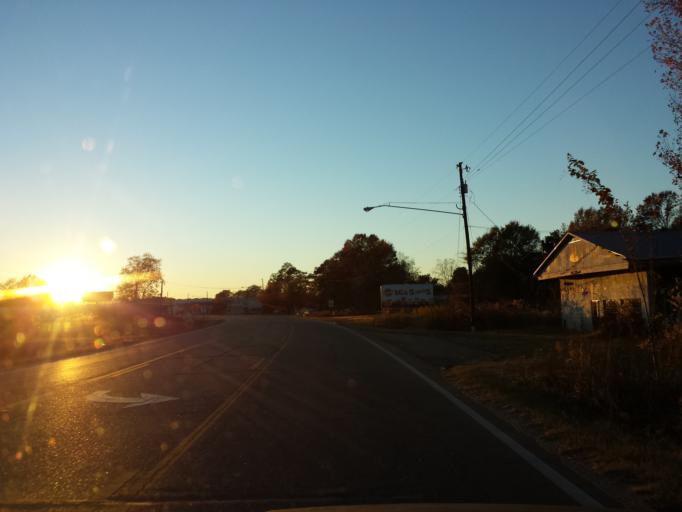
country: US
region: Mississippi
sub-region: Forrest County
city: Hattiesburg
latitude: 31.3436
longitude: -89.2978
